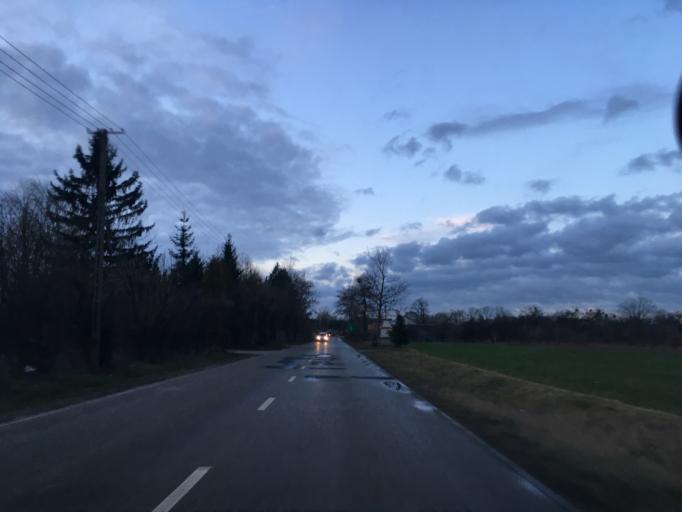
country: PL
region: Masovian Voivodeship
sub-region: Powiat pruszkowski
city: Owczarnia
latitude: 52.0765
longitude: 20.7040
